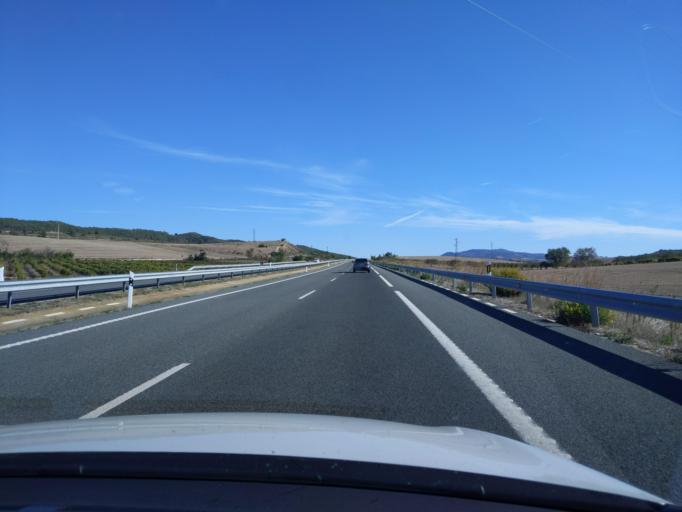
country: ES
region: Navarre
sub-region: Provincia de Navarra
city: Los Arcos
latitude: 42.5740
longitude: -2.1581
